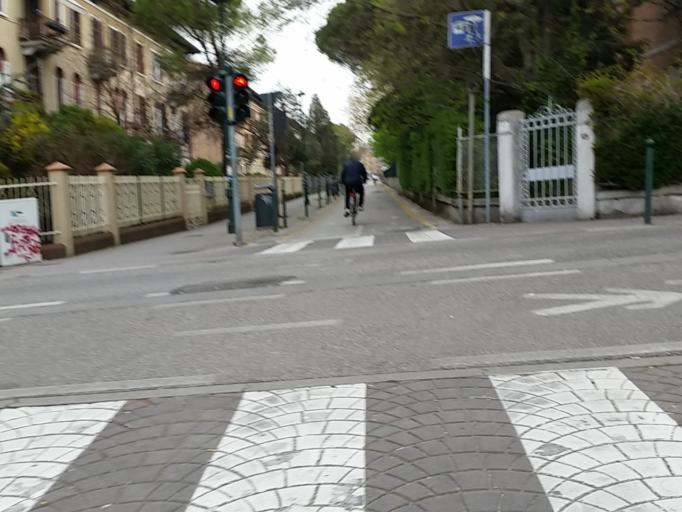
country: IT
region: Veneto
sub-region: Provincia di Venezia
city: Mestre
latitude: 45.4861
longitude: 12.2365
